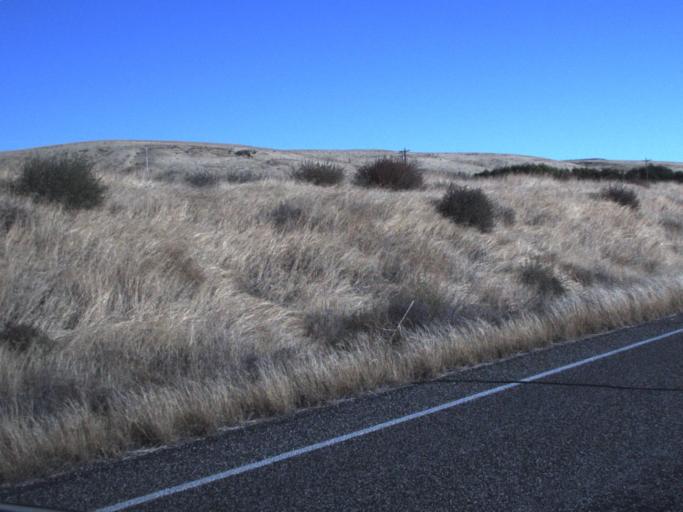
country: US
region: Washington
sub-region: Benton County
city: Benton City
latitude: 46.3461
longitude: -119.4709
